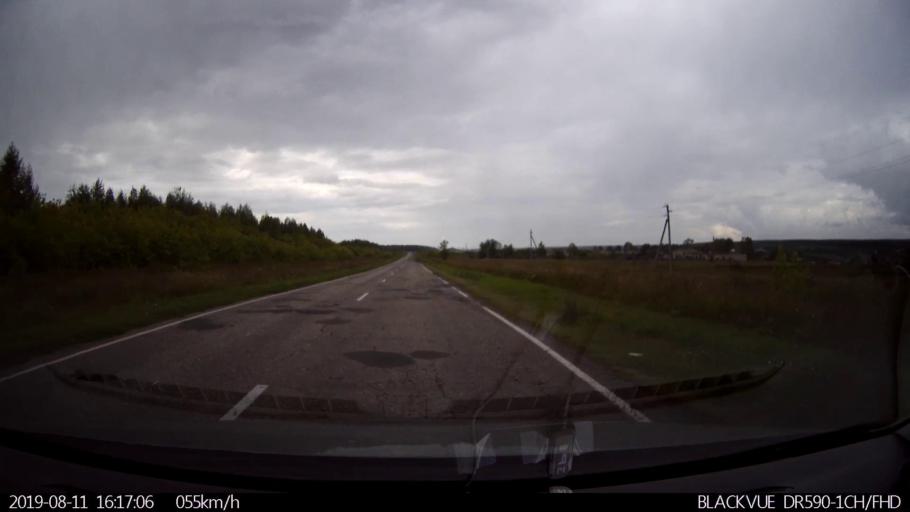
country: RU
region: Ulyanovsk
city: Mayna
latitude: 54.0460
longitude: 47.6180
